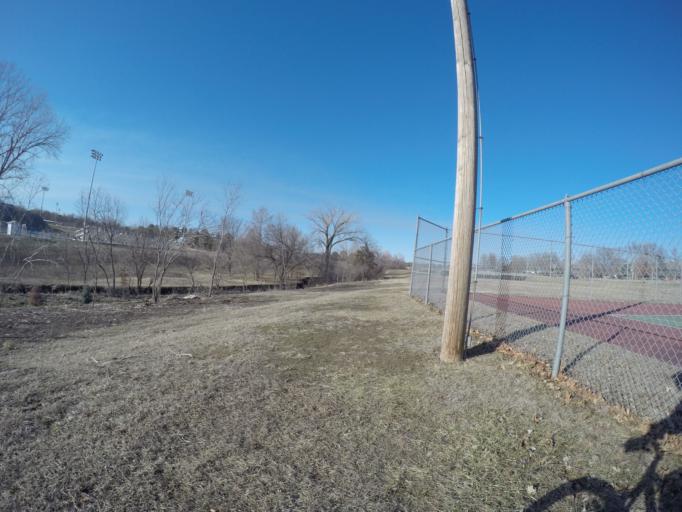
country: US
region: Kansas
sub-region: Riley County
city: Manhattan
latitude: 39.1994
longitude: -96.6180
